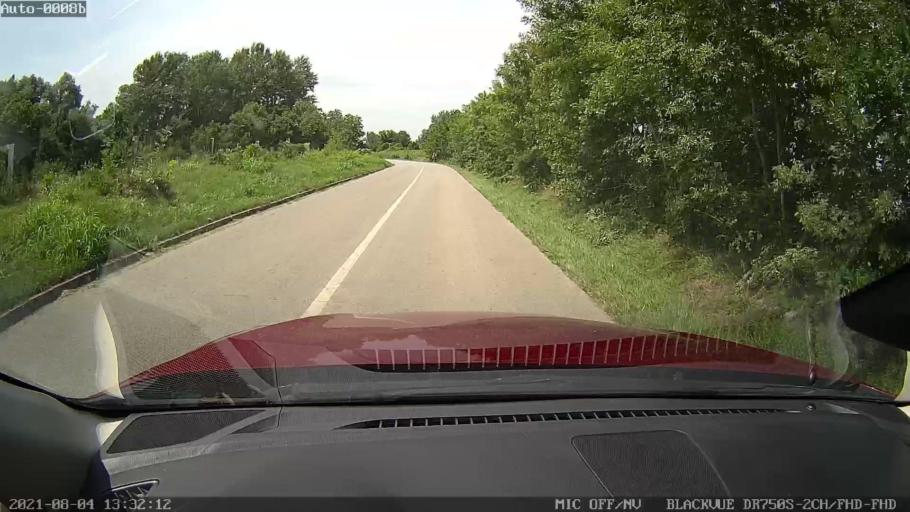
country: HR
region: Osjecko-Baranjska
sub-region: Grad Osijek
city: Bilje
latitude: 45.6073
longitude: 18.7633
